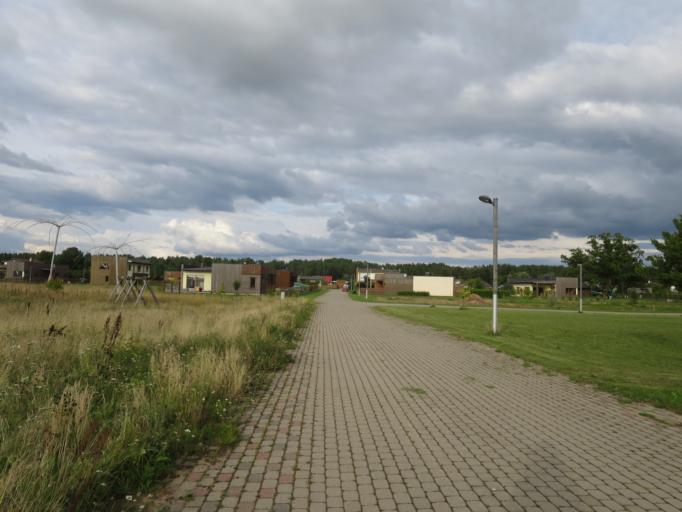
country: LV
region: Ikskile
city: Ikskile
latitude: 56.8345
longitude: 24.4764
